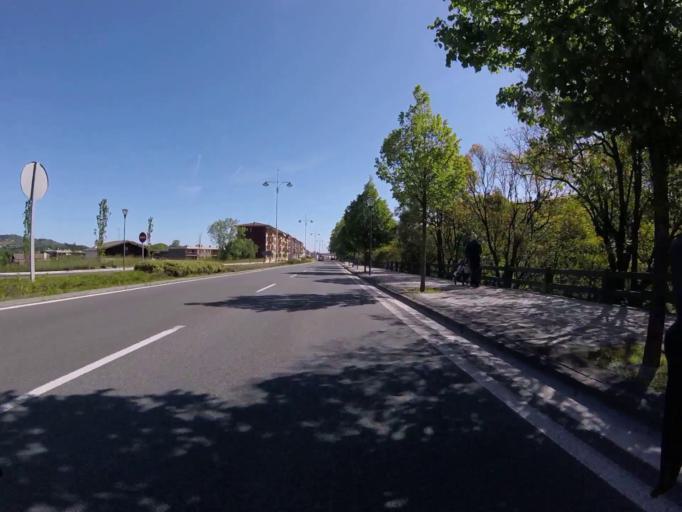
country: ES
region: Basque Country
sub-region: Provincia de Guipuzcoa
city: Irun
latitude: 43.3424
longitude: -1.8078
